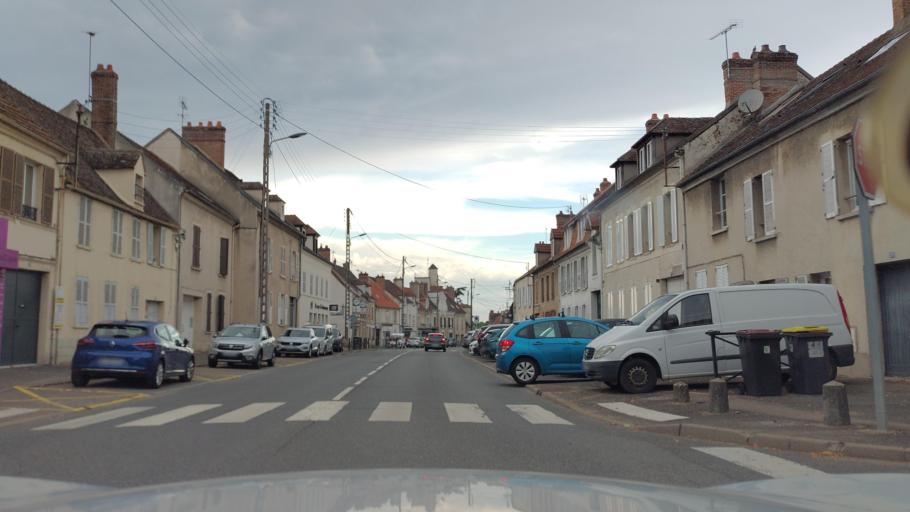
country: FR
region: Ile-de-France
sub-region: Departement de Seine-et-Marne
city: Guignes
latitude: 48.6351
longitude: 2.8005
